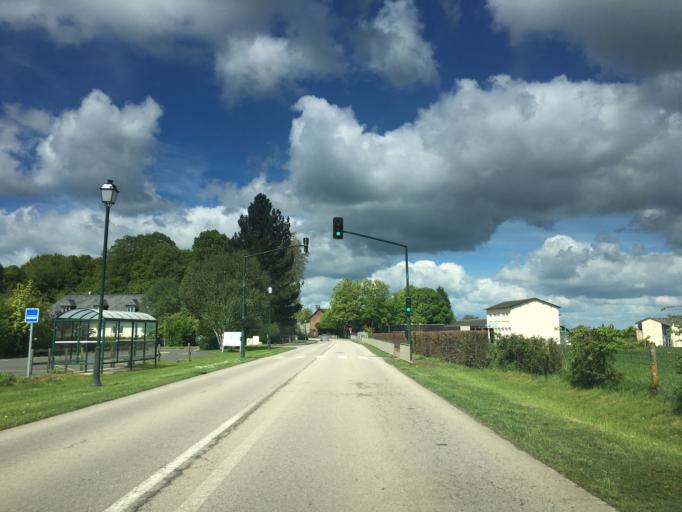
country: FR
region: Lower Normandy
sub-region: Departement de l'Orne
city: Aube-sur-Rile
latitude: 48.8404
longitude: 0.5169
